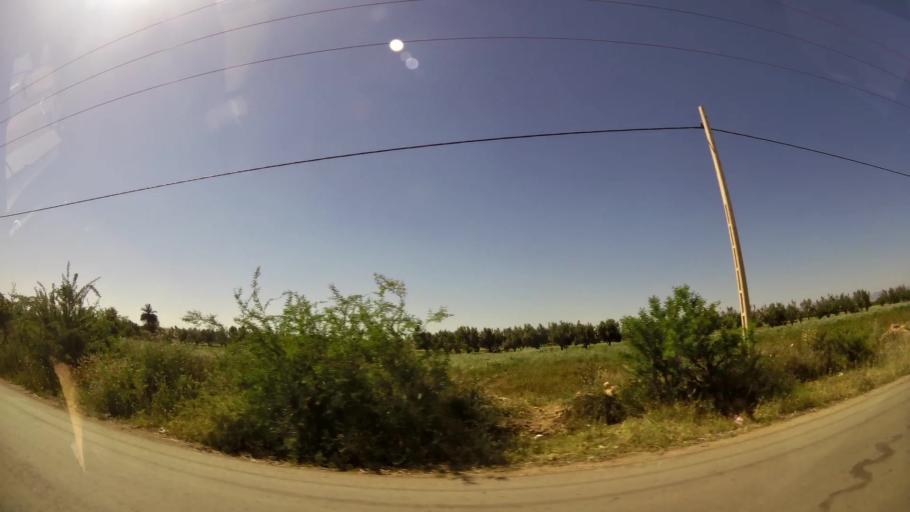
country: MA
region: Oriental
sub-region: Oujda-Angad
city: Oujda
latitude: 34.7026
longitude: -1.8724
